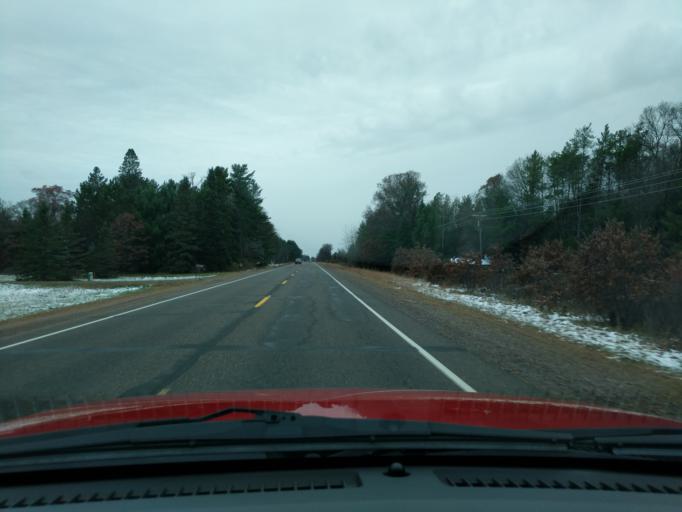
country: US
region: Wisconsin
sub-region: Burnett County
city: Siren
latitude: 45.8167
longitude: -92.3489
